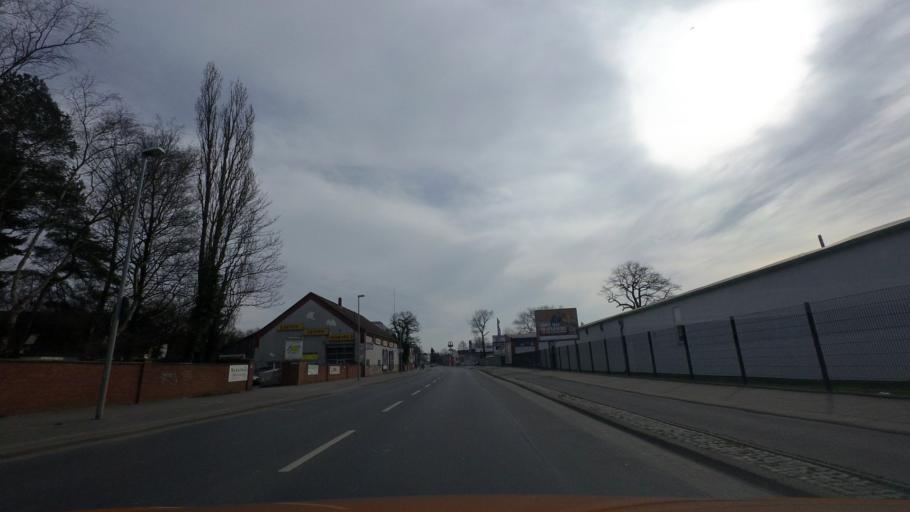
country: DE
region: Lower Saxony
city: Isernhagen Farster Bauerschaft
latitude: 52.3833
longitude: 9.8610
